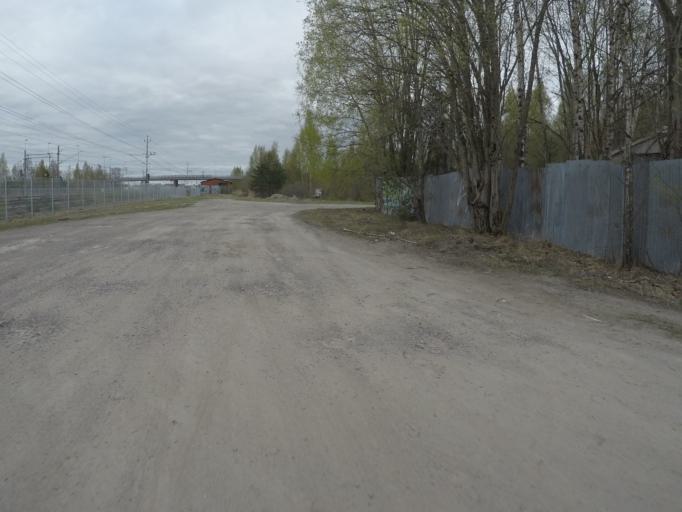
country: SE
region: Soedermanland
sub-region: Eskilstuna Kommun
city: Hallbybrunn
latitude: 59.4025
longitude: 16.4142
